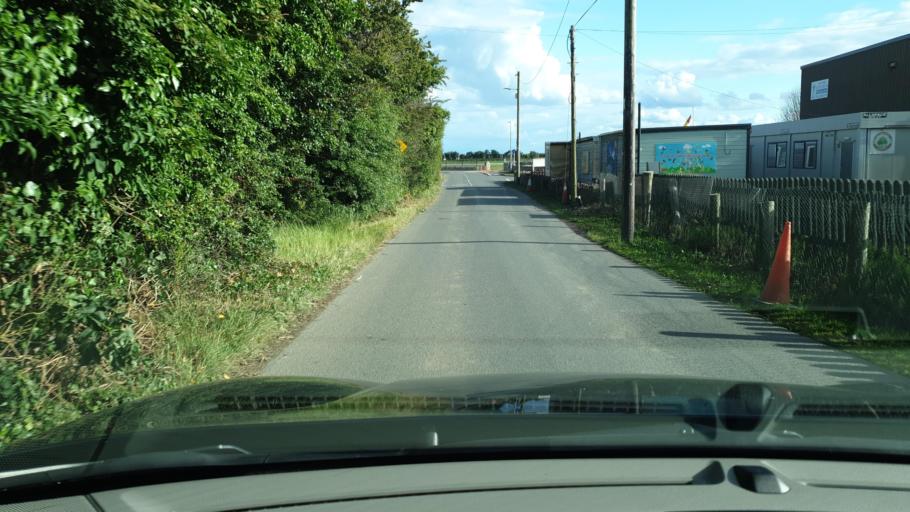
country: IE
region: Leinster
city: An Ros
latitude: 53.5326
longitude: -6.1054
